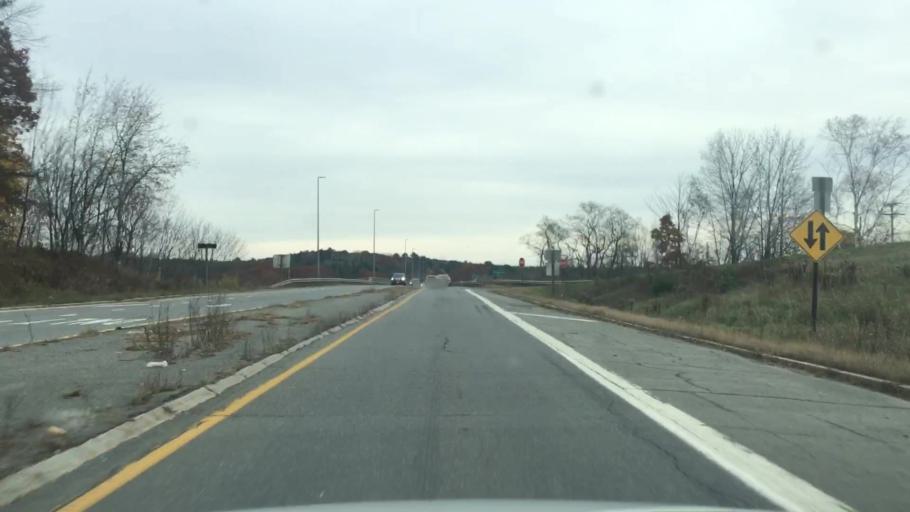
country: US
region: Maine
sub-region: Waldo County
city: Belfast
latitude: 44.4322
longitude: -69.0147
